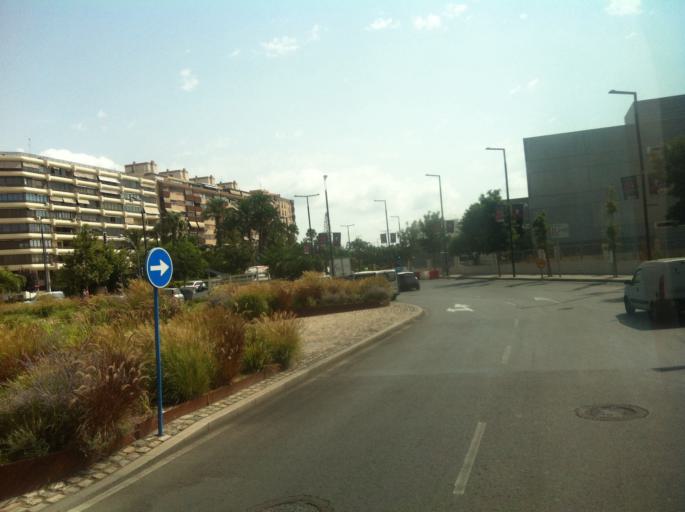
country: ES
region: Valencia
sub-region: Provincia de Alicante
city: Alicante
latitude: 38.3375
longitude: -0.4931
